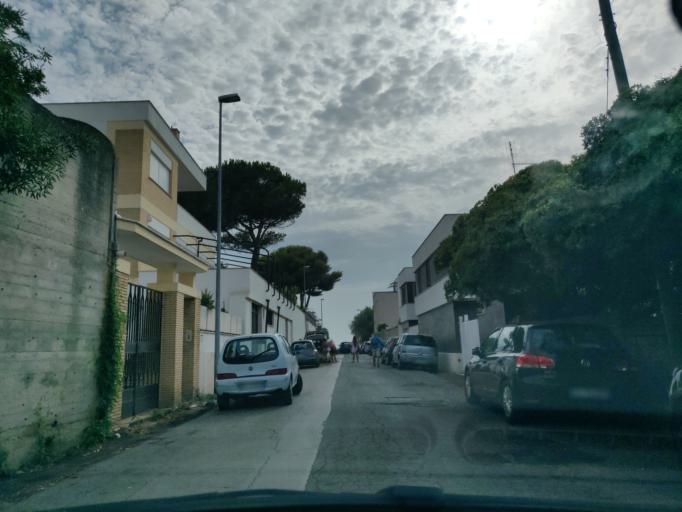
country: IT
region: Latium
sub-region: Citta metropolitana di Roma Capitale
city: Civitavecchia
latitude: 42.0749
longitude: 11.8075
